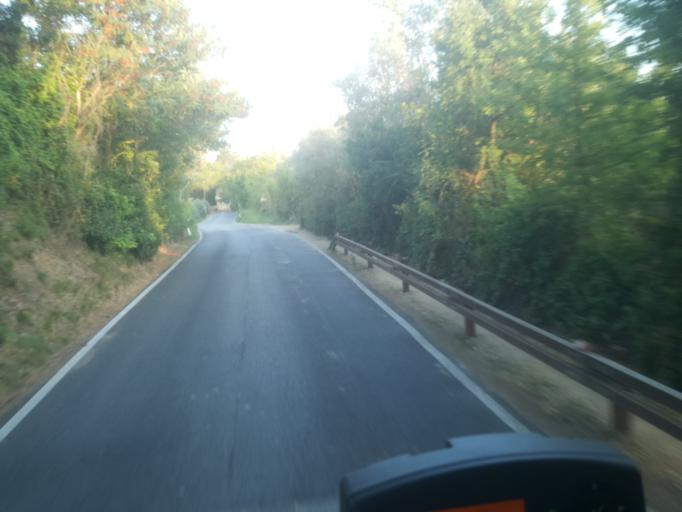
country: IT
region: Tuscany
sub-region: Province of Florence
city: Gambassi Terme
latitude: 43.5403
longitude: 10.9608
